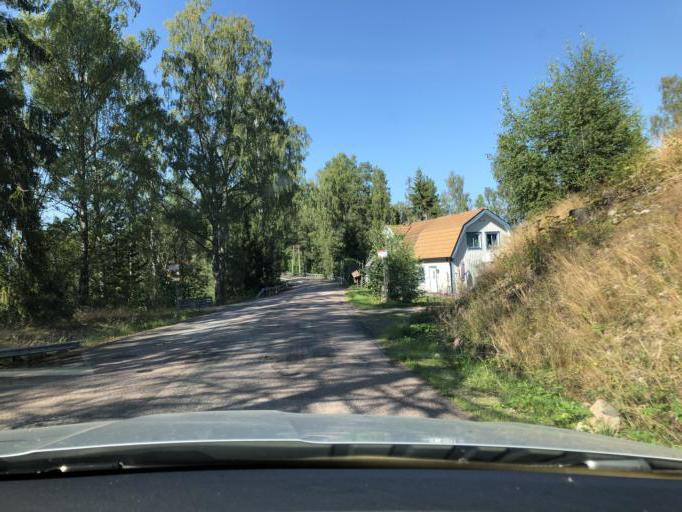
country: SE
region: Dalarna
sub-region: Hedemora Kommun
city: Hedemora
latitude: 60.3599
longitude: 15.9268
